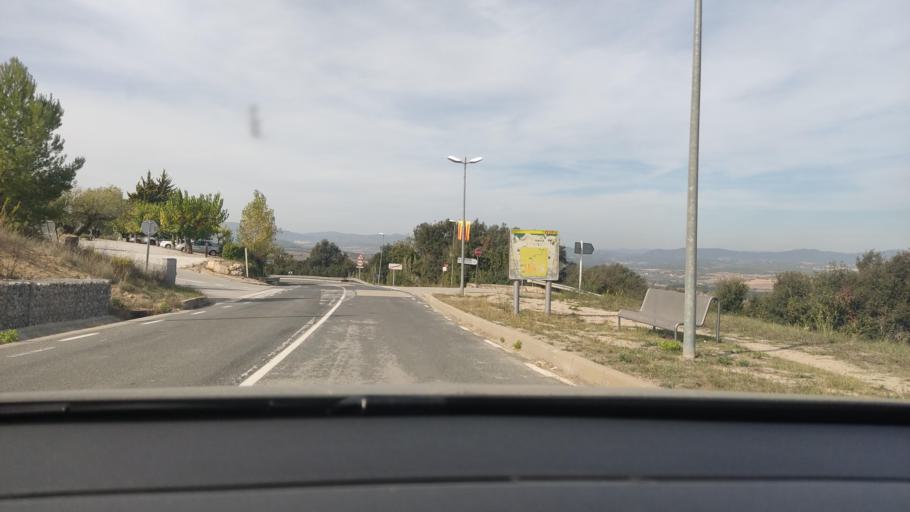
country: ES
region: Catalonia
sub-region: Provincia de Barcelona
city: Sant Sadurni d'Anoia
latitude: 41.4093
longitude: 1.8081
